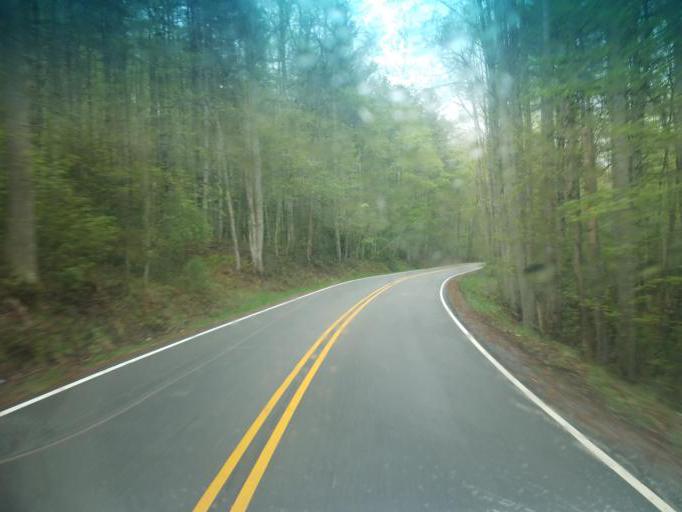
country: US
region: Virginia
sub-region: Washington County
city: Glade Spring
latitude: 36.6393
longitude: -81.7462
